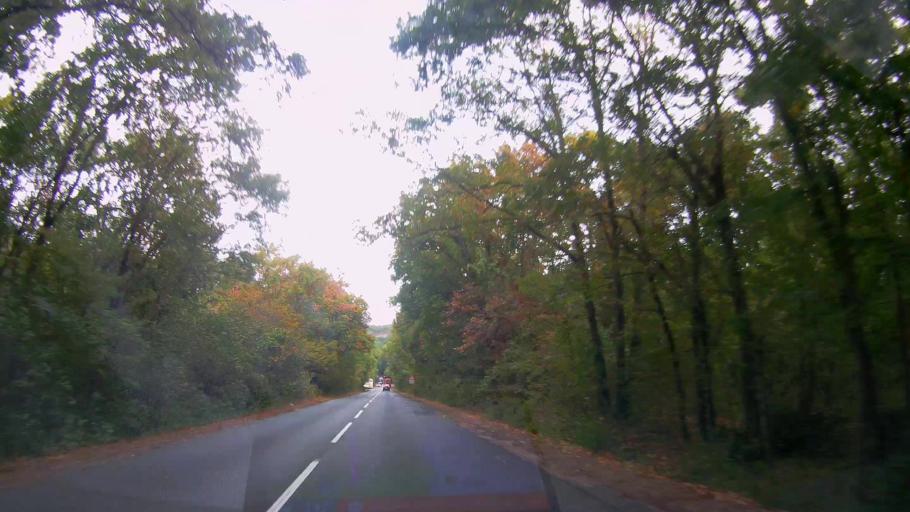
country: BG
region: Burgas
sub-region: Obshtina Primorsko
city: Primorsko
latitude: 42.2983
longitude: 27.7296
